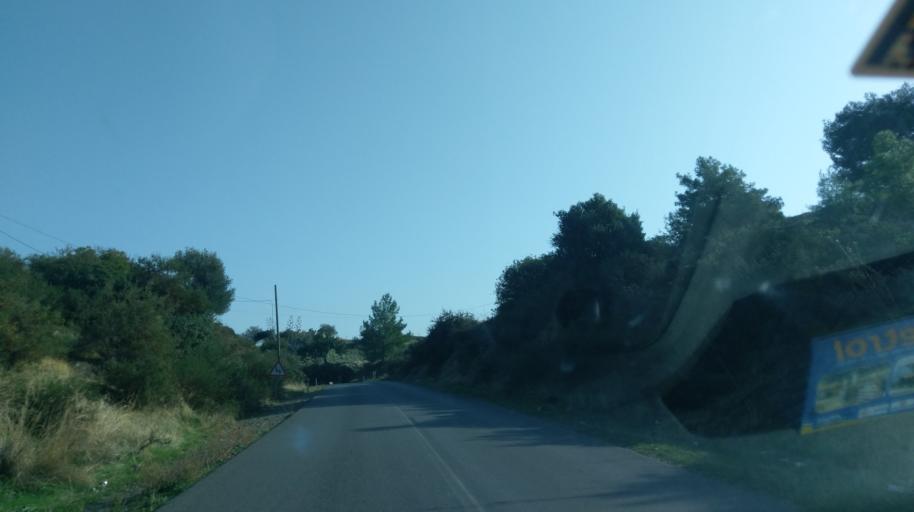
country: CY
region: Lefkosia
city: Kato Pyrgos
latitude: 35.1586
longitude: 32.7557
